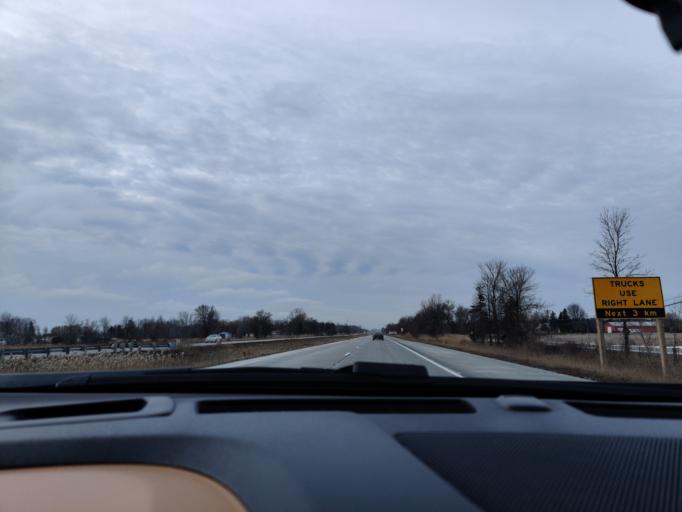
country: CA
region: Quebec
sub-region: Monteregie
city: Les Coteaux
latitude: 45.1623
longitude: -74.4453
